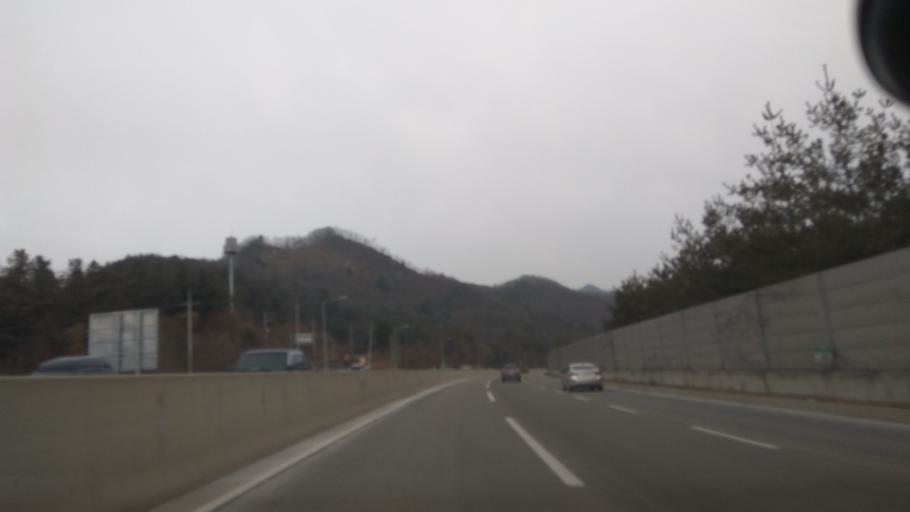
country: KR
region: Gyeonggi-do
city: Cheongpyeong
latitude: 37.6484
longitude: 127.4257
